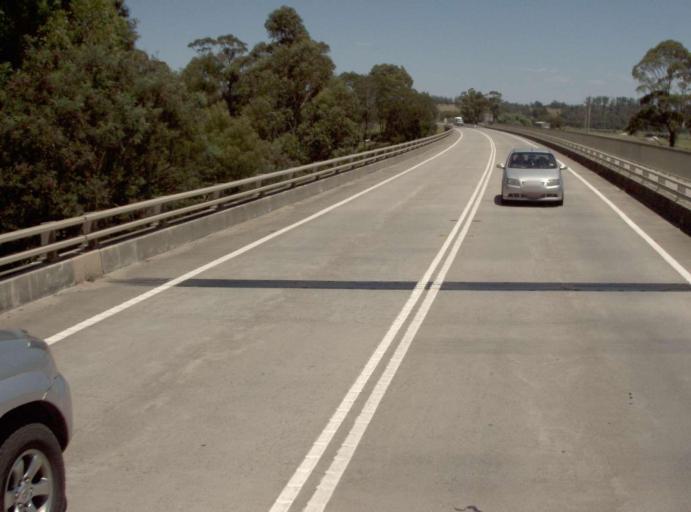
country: AU
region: Victoria
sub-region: East Gippsland
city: Lakes Entrance
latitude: -37.7147
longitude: 148.4545
